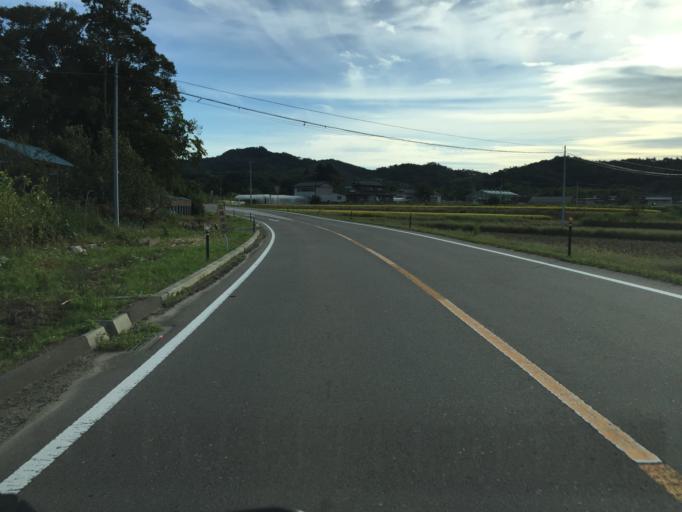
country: JP
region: Fukushima
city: Yanagawamachi-saiwaicho
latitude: 37.8323
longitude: 140.6148
